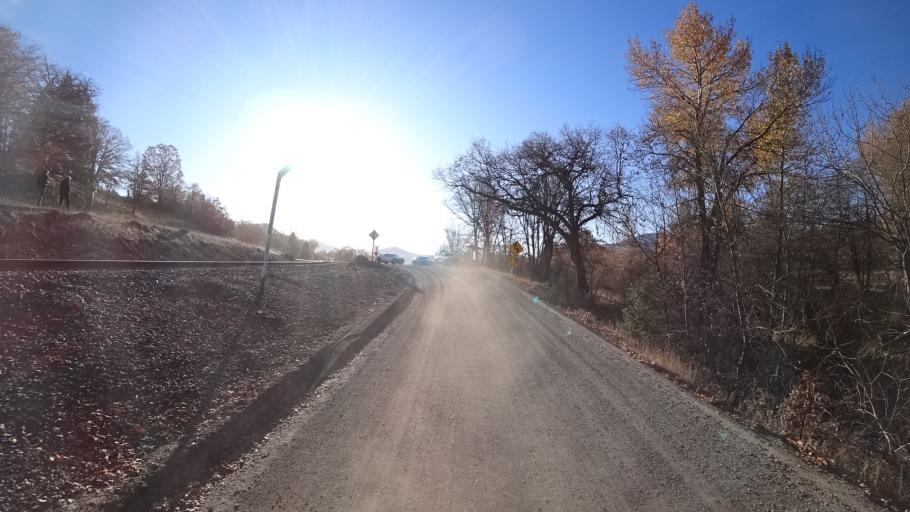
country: US
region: Oregon
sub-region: Jackson County
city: Ashland
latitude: 42.0049
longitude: -122.6454
